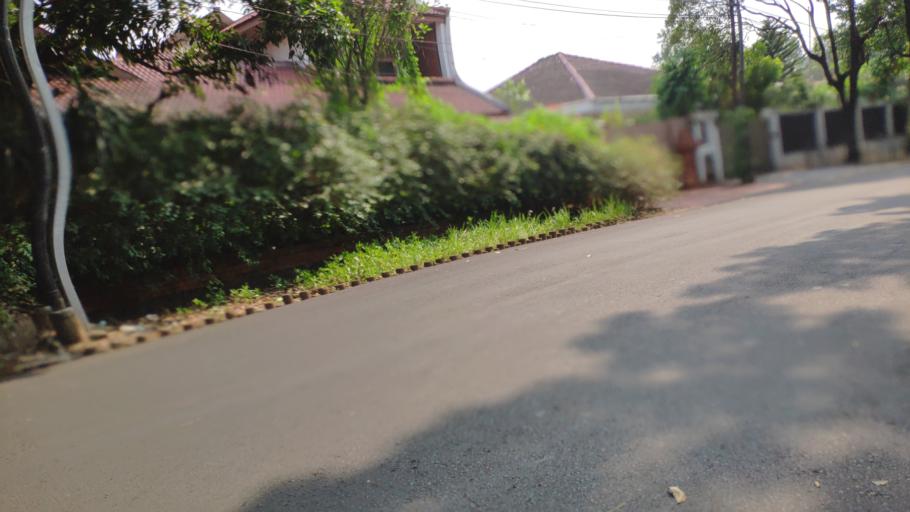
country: ID
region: Jakarta Raya
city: Jakarta
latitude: -6.2687
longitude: 106.8193
